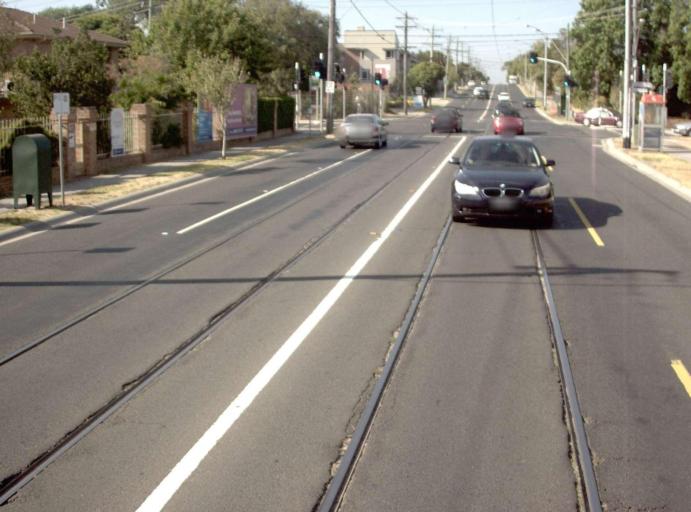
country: AU
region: Victoria
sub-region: Bayside
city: Brighton East
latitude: -37.9081
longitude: 145.0179
